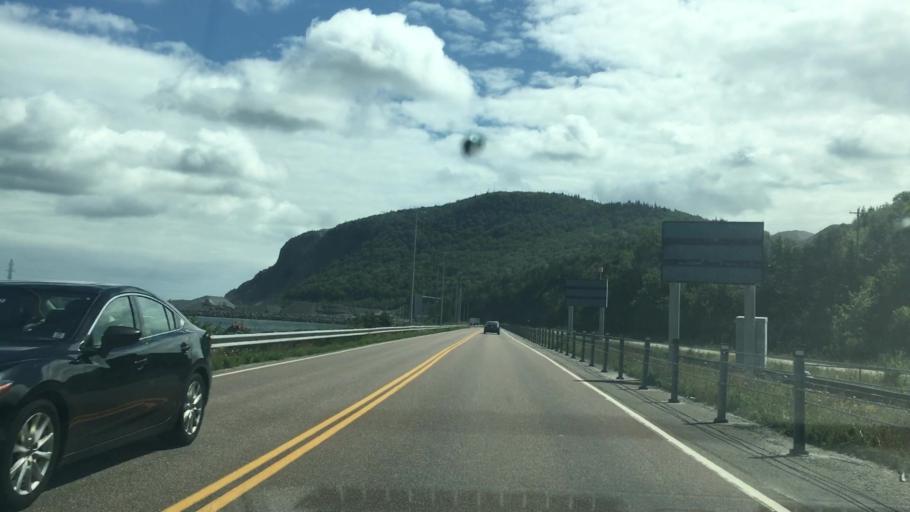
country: CA
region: Nova Scotia
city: Port Hawkesbury
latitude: 45.6449
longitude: -61.4341
